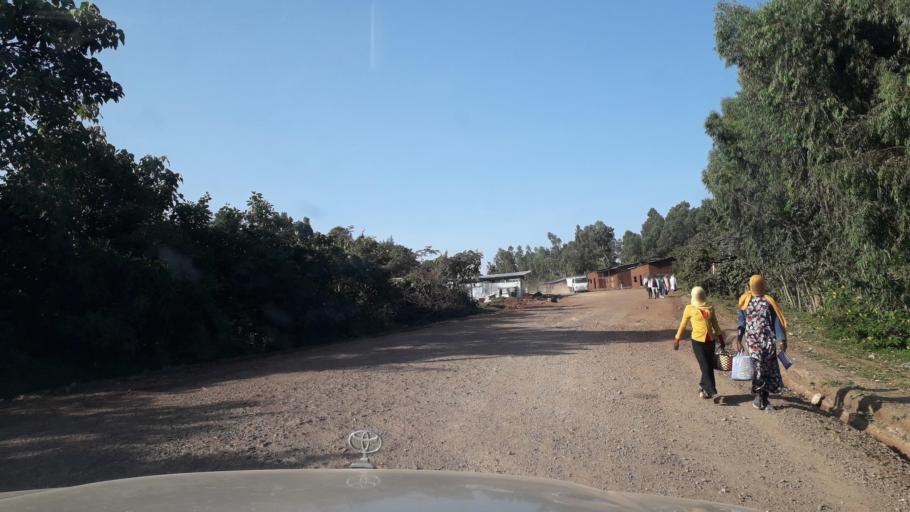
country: ET
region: Oromiya
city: Jima
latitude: 7.4876
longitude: 36.8804
